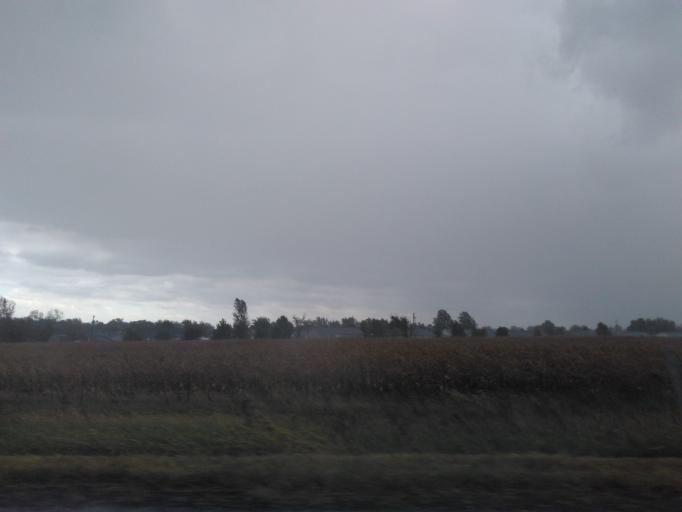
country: US
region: Illinois
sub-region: Madison County
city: Highland
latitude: 38.7869
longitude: -89.6256
